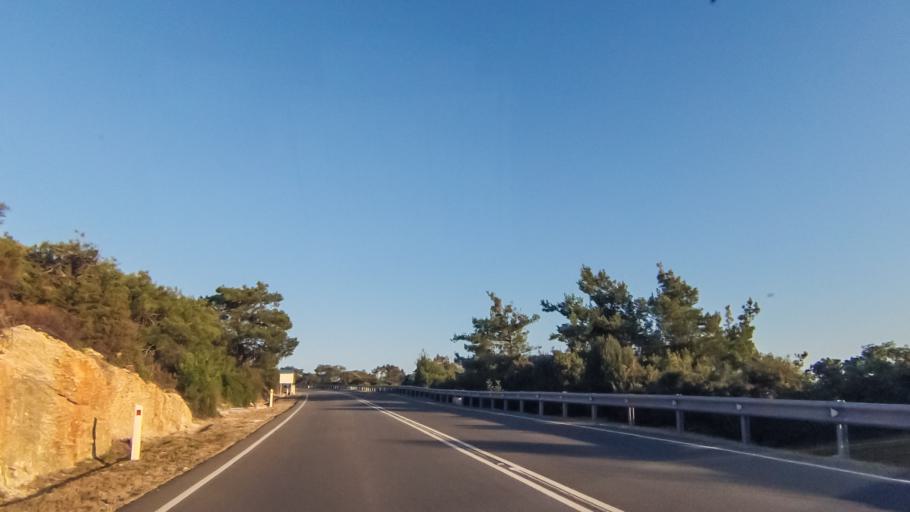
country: CY
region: Limassol
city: Sotira
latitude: 34.6747
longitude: 32.8518
